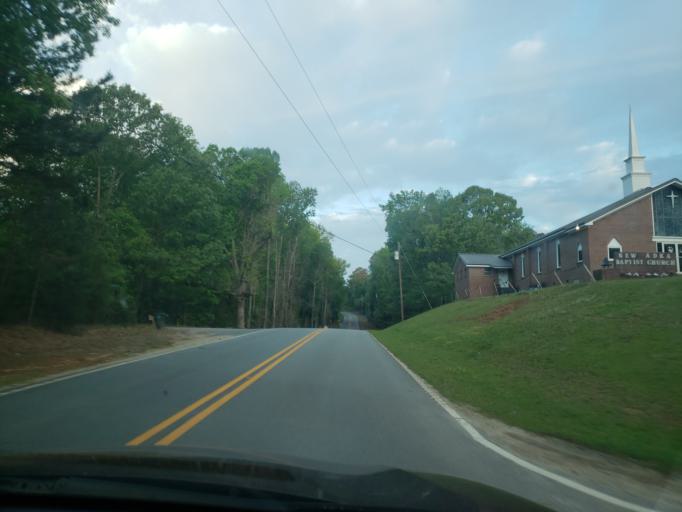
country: US
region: Alabama
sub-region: Tallapoosa County
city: Dadeville
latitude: 32.7020
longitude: -85.7481
